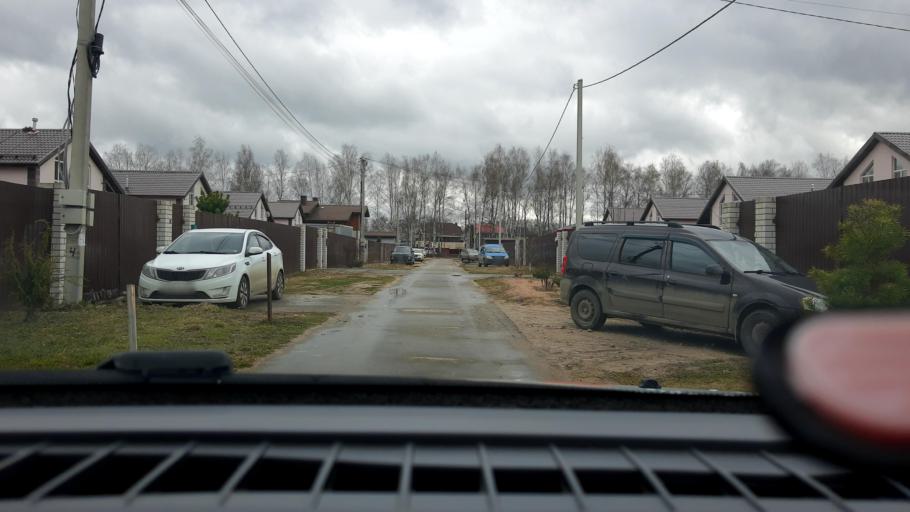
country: RU
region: Nizjnij Novgorod
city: Neklyudovo
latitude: 56.4100
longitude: 44.0216
